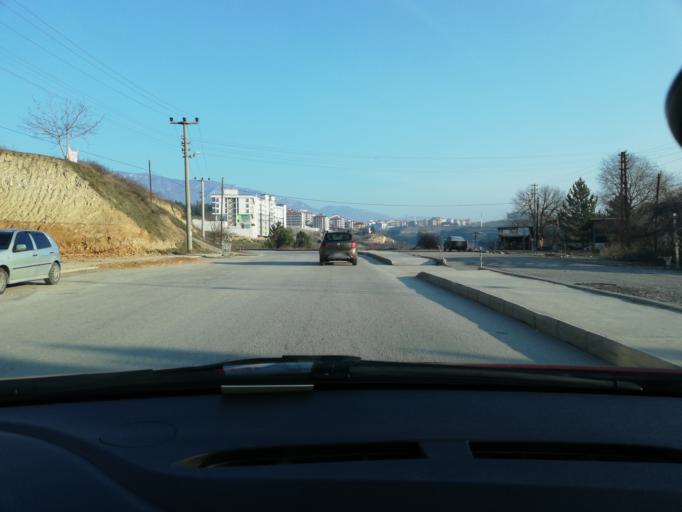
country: TR
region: Karabuk
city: Safranbolu
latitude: 41.2251
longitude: 32.6706
